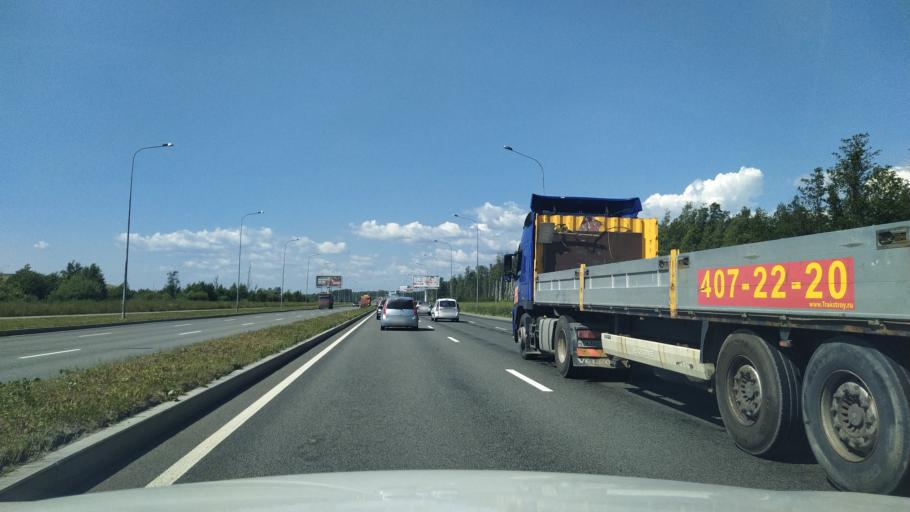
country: RU
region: St.-Petersburg
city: Levashovo
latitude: 60.0667
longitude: 30.1902
